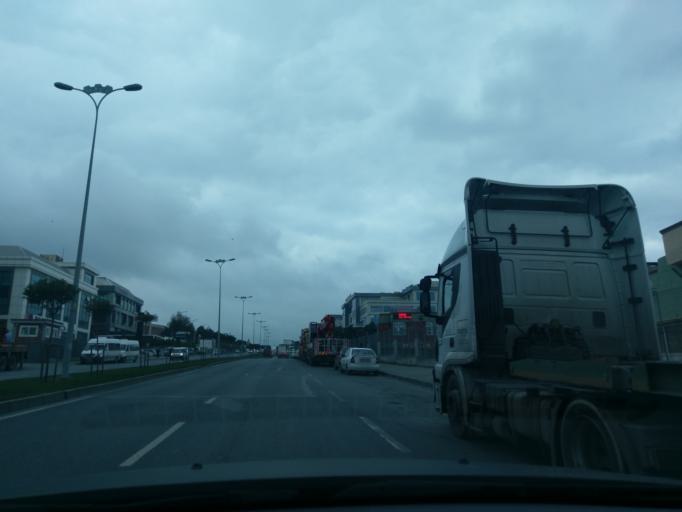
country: TR
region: Istanbul
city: Basaksehir
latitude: 41.0745
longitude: 28.8001
